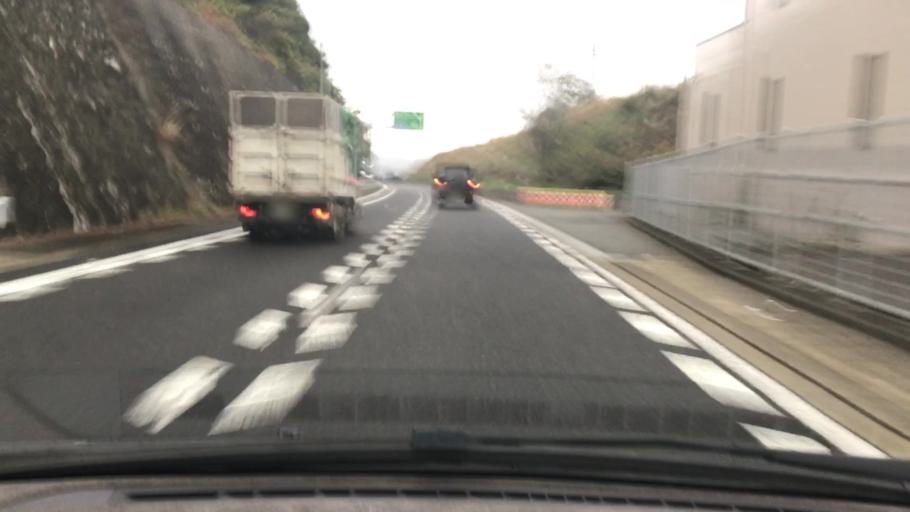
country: JP
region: Hyogo
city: Sandacho
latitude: 34.8105
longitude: 135.2471
